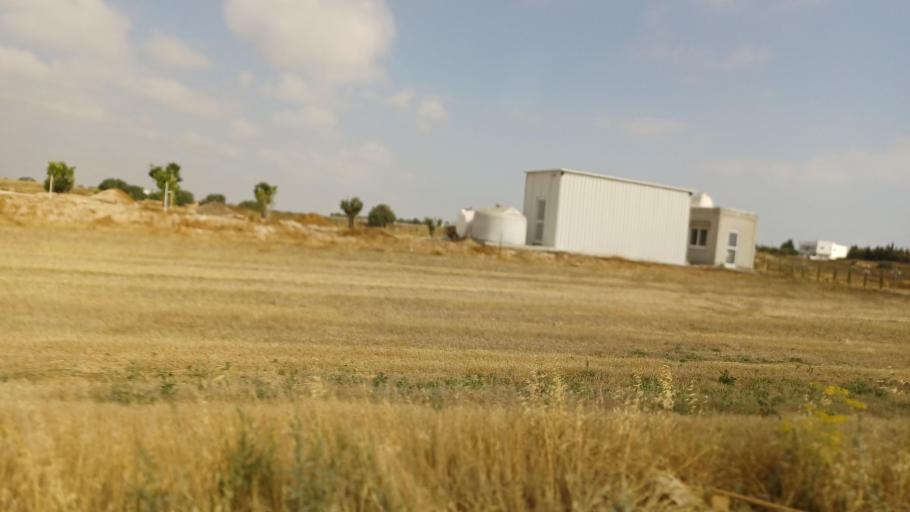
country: CY
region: Ammochostos
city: Paralimni
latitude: 35.0241
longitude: 34.0072
